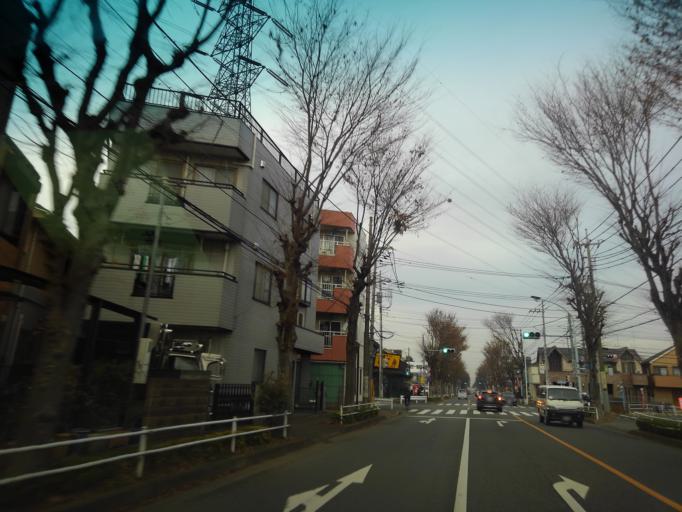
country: JP
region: Tokyo
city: Higashimurayama-shi
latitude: 35.7380
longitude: 139.4449
